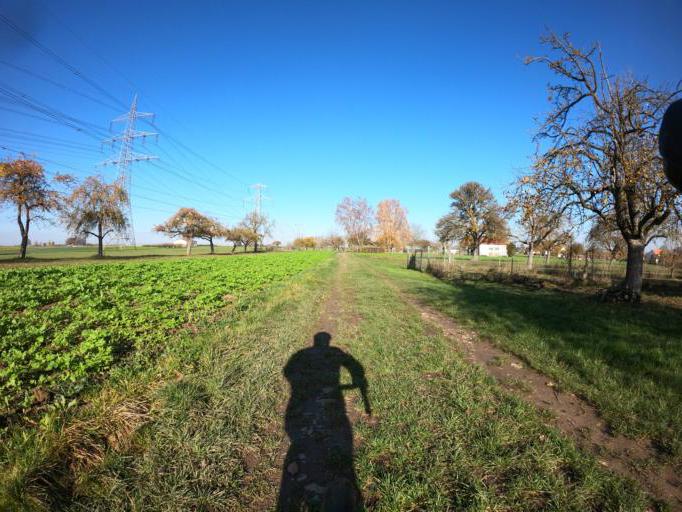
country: DE
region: Baden-Wuerttemberg
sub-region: Regierungsbezirk Stuttgart
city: Magstadt
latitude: 48.7258
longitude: 8.9549
